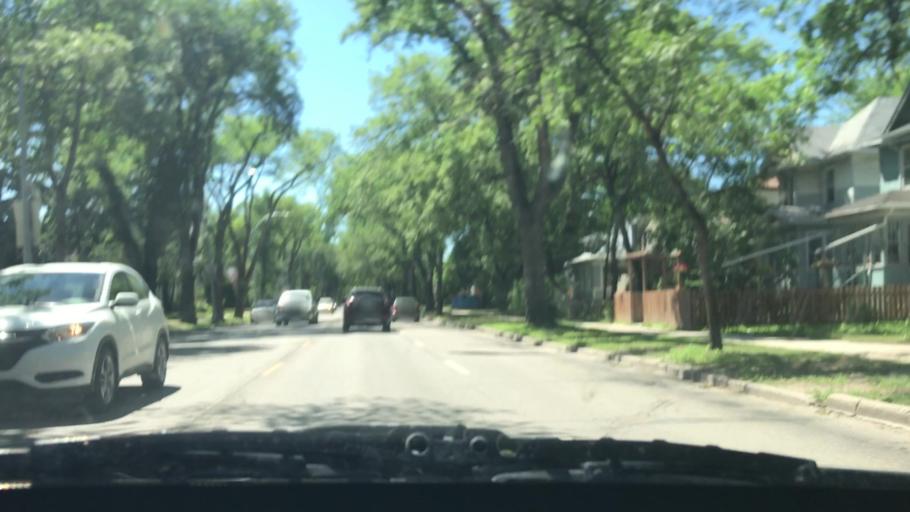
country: CA
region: Manitoba
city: Winnipeg
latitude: 49.8590
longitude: -97.1323
